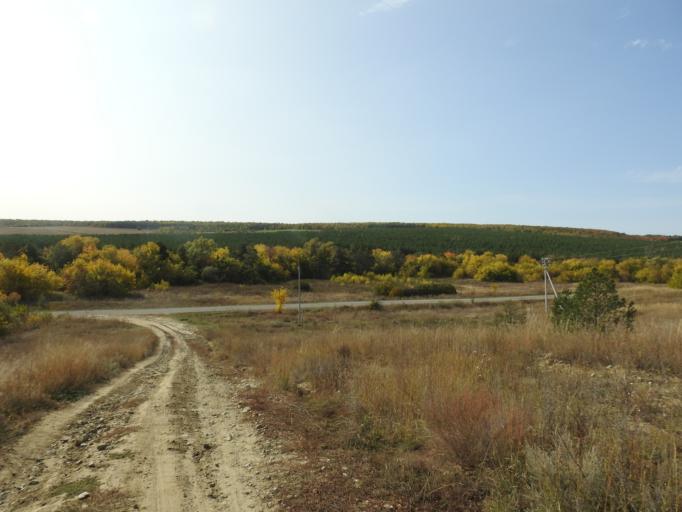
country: RU
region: Saratov
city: Baltay
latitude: 52.5008
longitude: 46.6605
